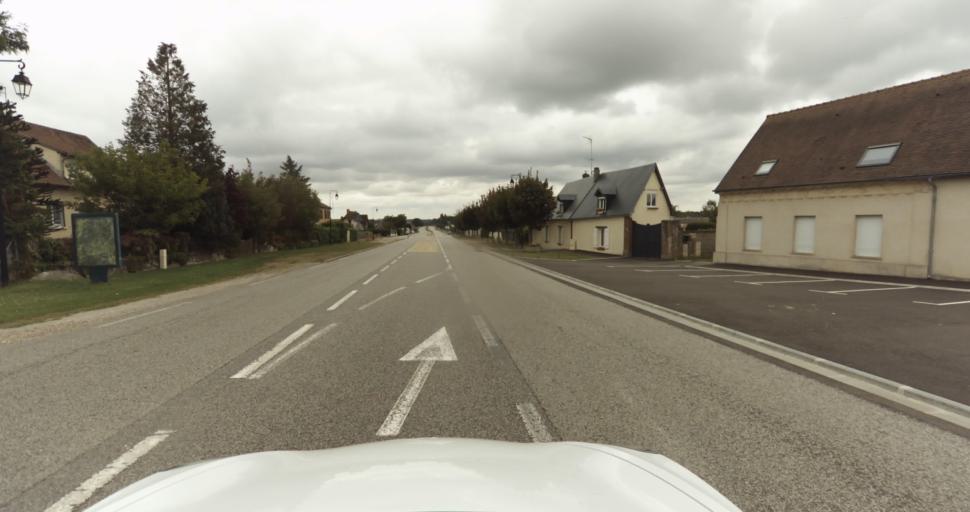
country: FR
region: Haute-Normandie
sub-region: Departement de l'Eure
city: Saint-Sebastien-de-Morsent
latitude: 49.0342
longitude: 1.0961
